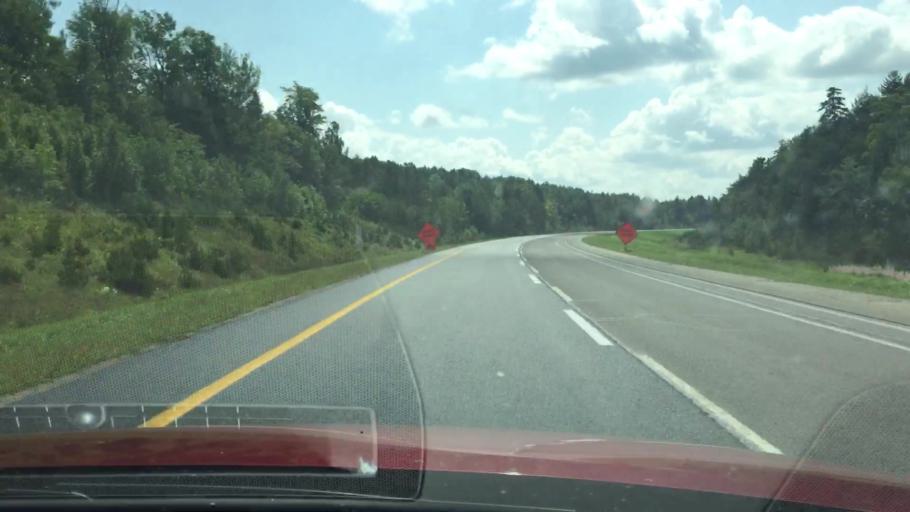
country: US
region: Maine
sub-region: Penobscot County
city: Medway
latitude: 45.7116
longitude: -68.4762
